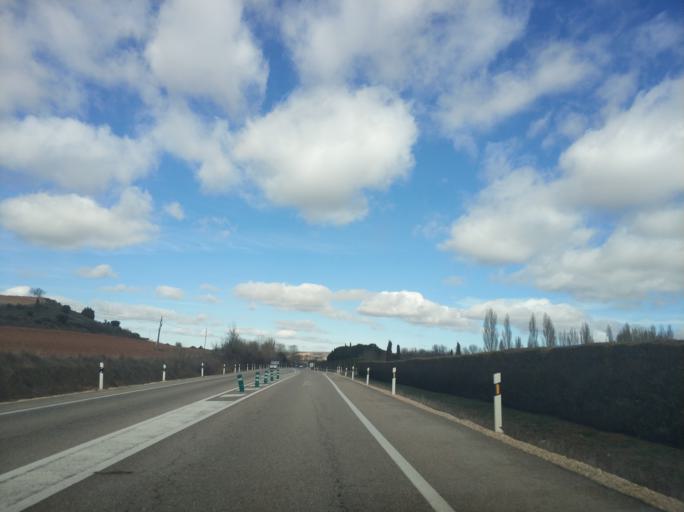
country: ES
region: Castille and Leon
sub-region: Provincia de Burgos
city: Sarracin
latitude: 42.2524
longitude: -3.6873
